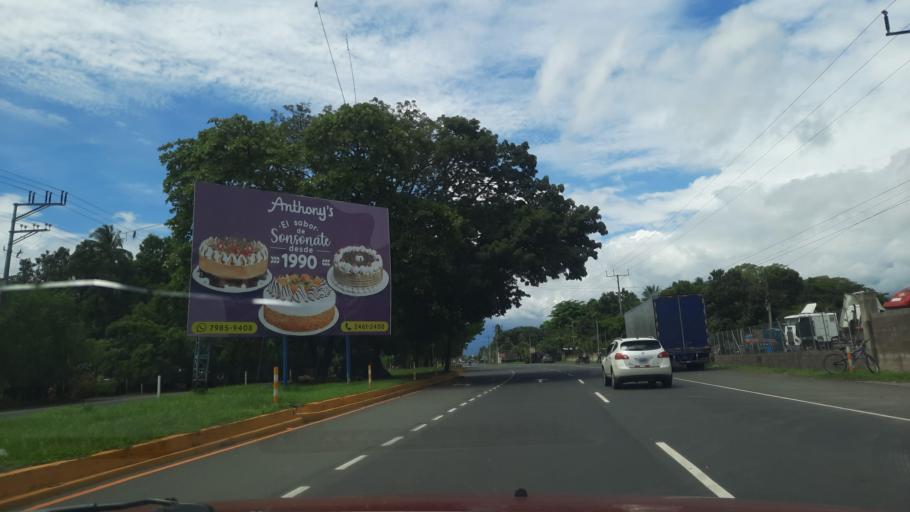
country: SV
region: Sonsonate
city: Acajutla
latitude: 13.6457
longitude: -89.7713
